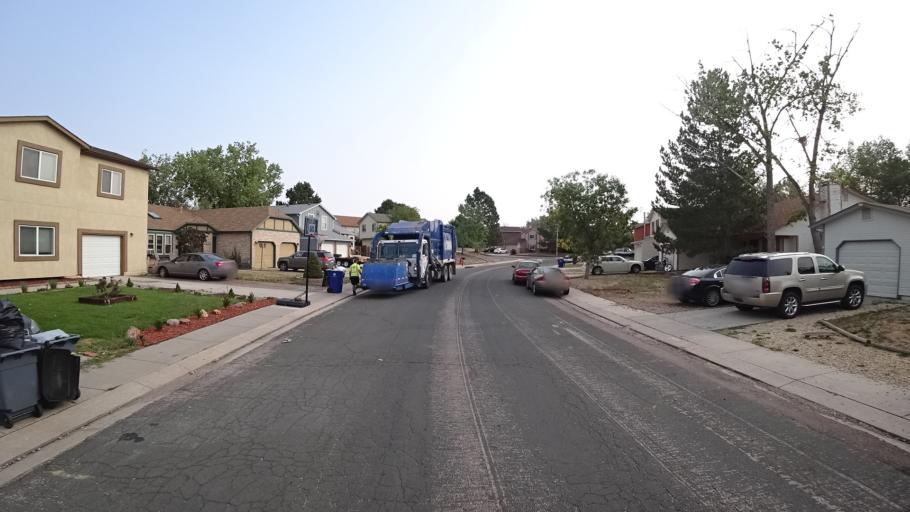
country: US
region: Colorado
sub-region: El Paso County
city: Stratmoor
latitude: 38.8073
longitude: -104.7496
